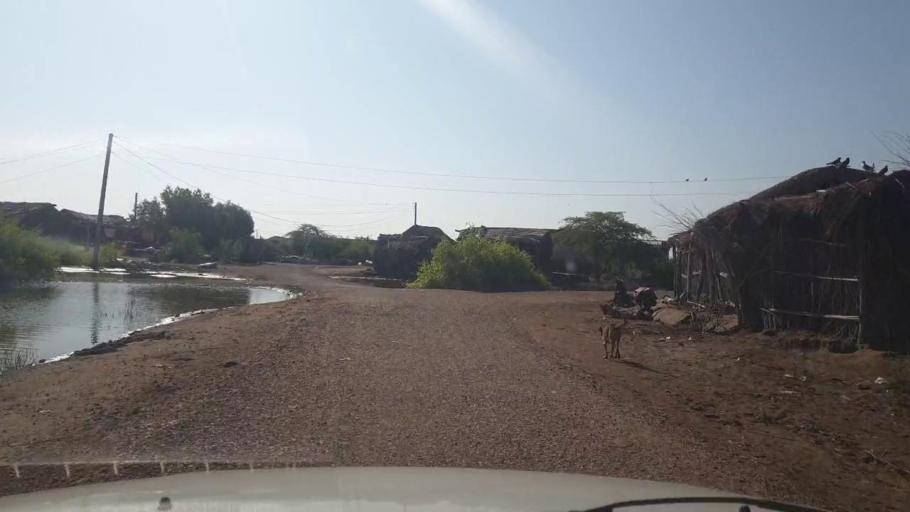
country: PK
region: Sindh
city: Chuhar Jamali
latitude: 24.4617
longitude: 67.9149
